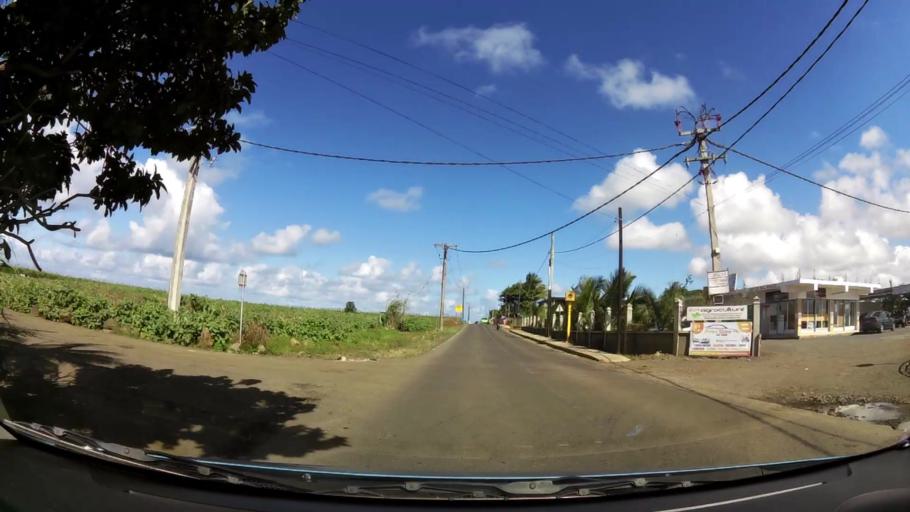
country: MU
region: Grand Port
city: Plaine Magnien
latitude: -20.4363
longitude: 57.6579
